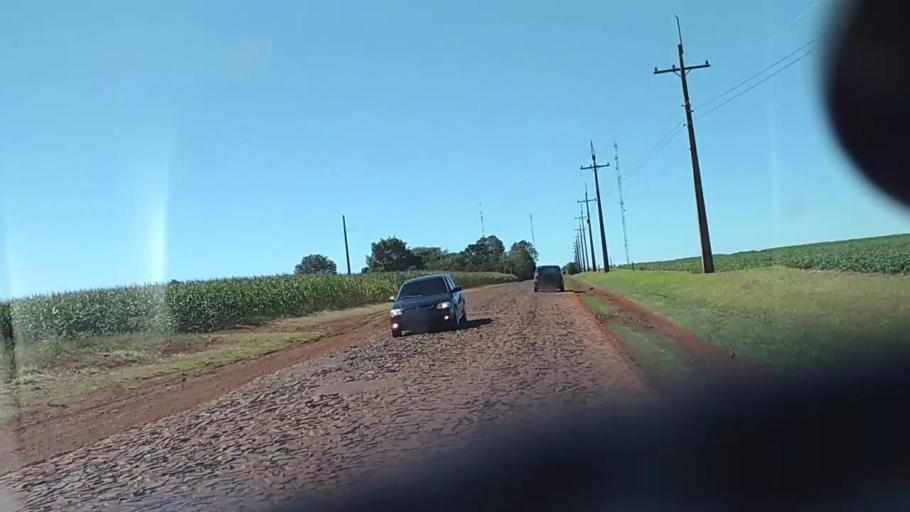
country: PY
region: Alto Parana
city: Naranjal
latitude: -25.9765
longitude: -55.1711
